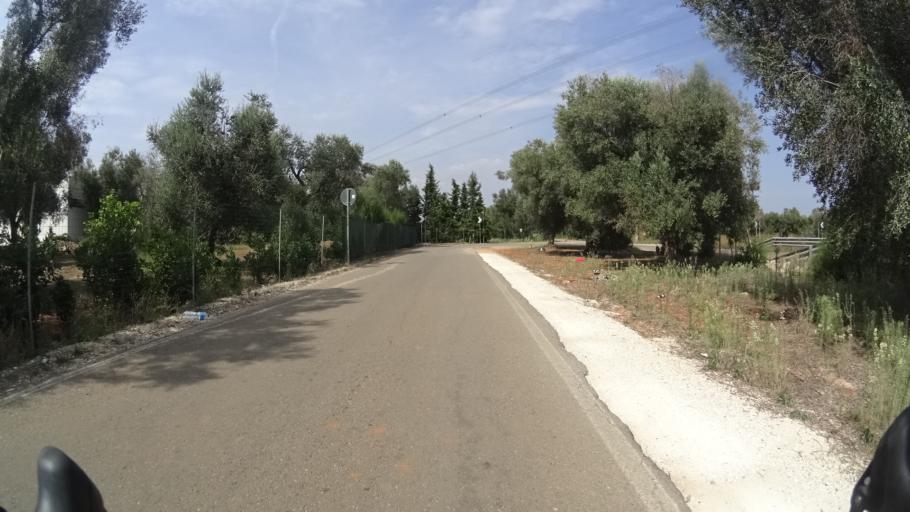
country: IT
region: Apulia
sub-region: Provincia di Lecce
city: Porto Cesareo
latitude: 40.2764
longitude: 17.9376
